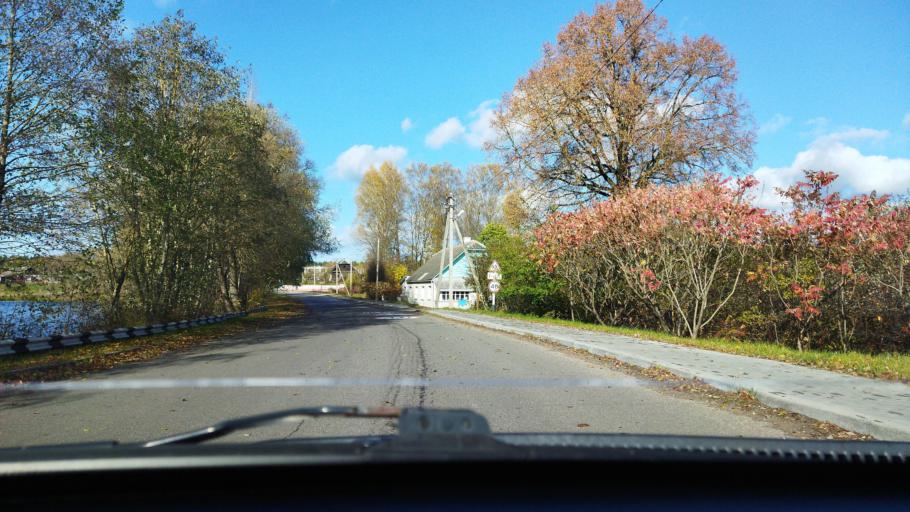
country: BY
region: Minsk
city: Svir
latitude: 54.8061
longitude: 26.2357
